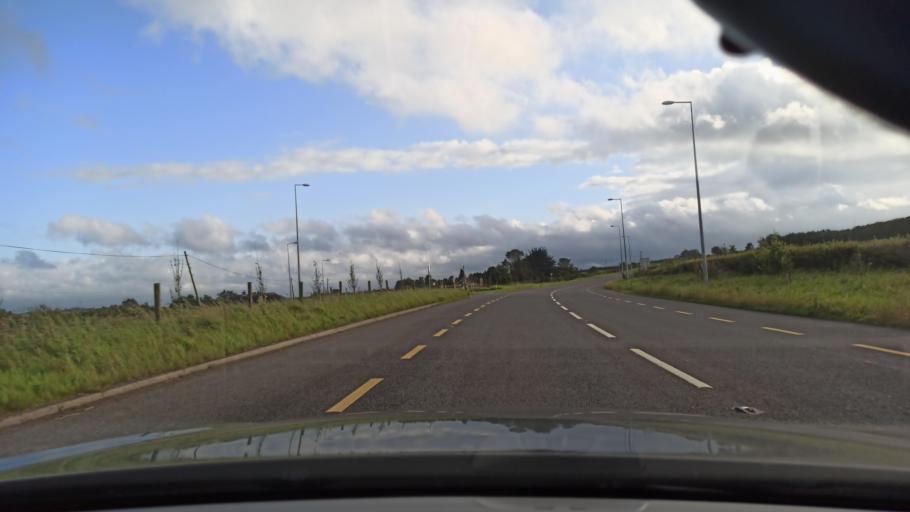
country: IE
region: Munster
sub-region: North Tipperary
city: Roscrea
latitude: 52.9287
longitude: -7.7889
